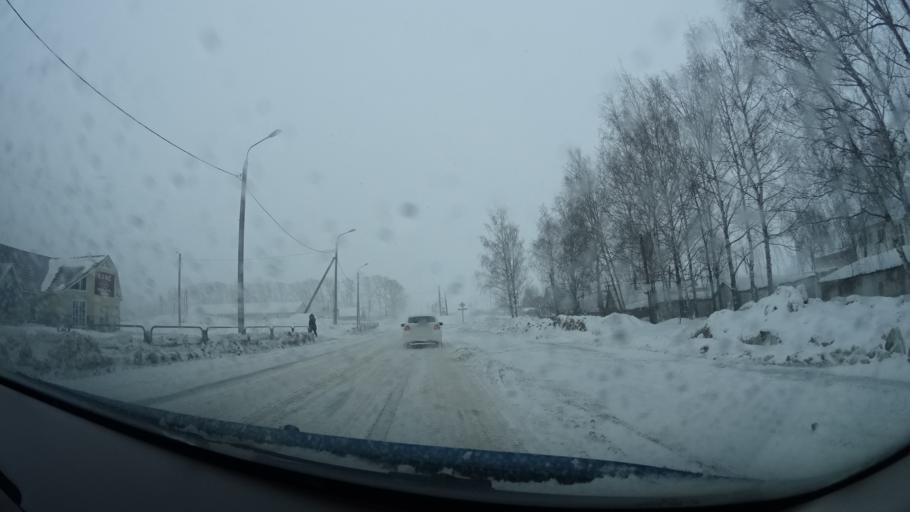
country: RU
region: Perm
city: Kuyeda
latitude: 56.4233
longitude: 55.5830
